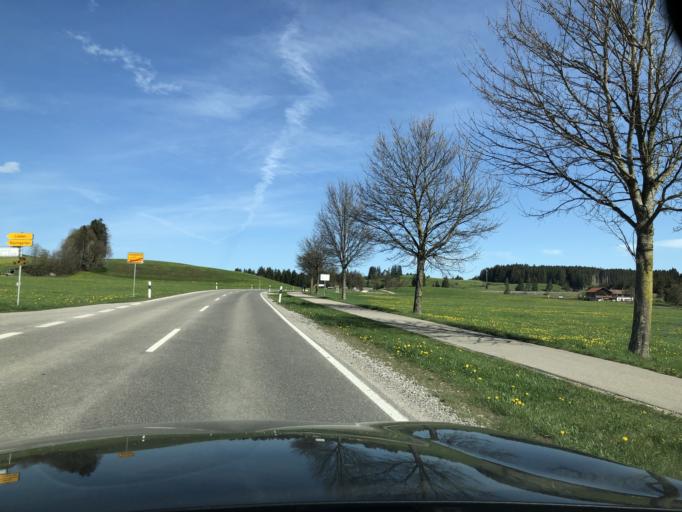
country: DE
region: Bavaria
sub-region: Swabia
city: Eisenberg
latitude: 47.6207
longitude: 10.6081
